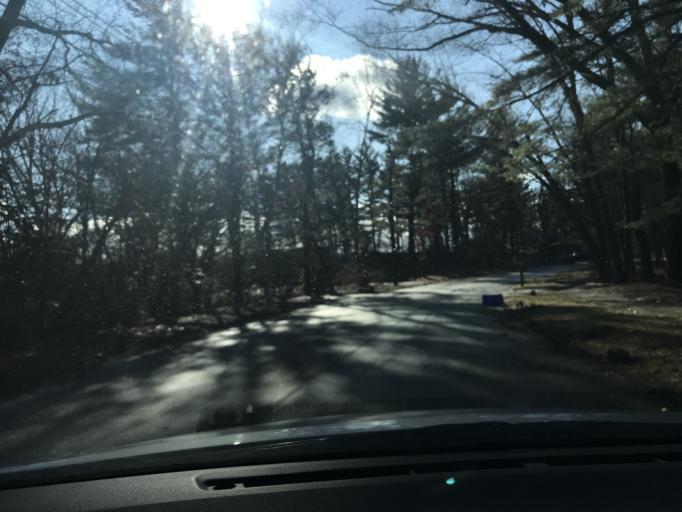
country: US
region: Massachusetts
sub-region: Middlesex County
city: Lexington
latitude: 42.4763
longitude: -71.2267
